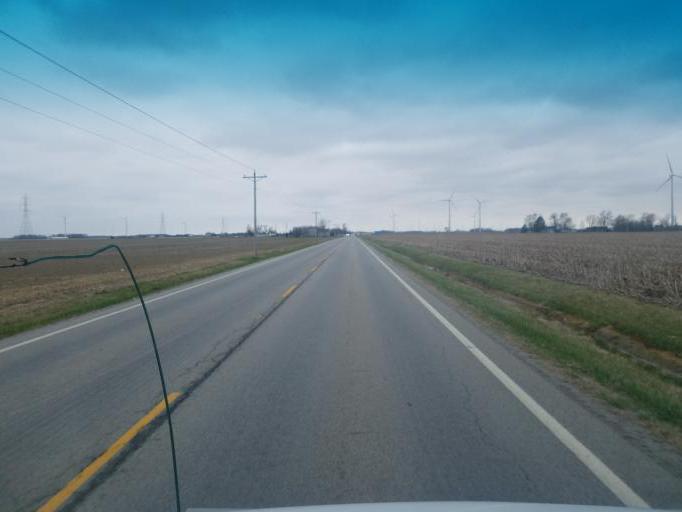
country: US
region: Ohio
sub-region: Van Wert County
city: Van Wert
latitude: 40.9317
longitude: -84.5065
